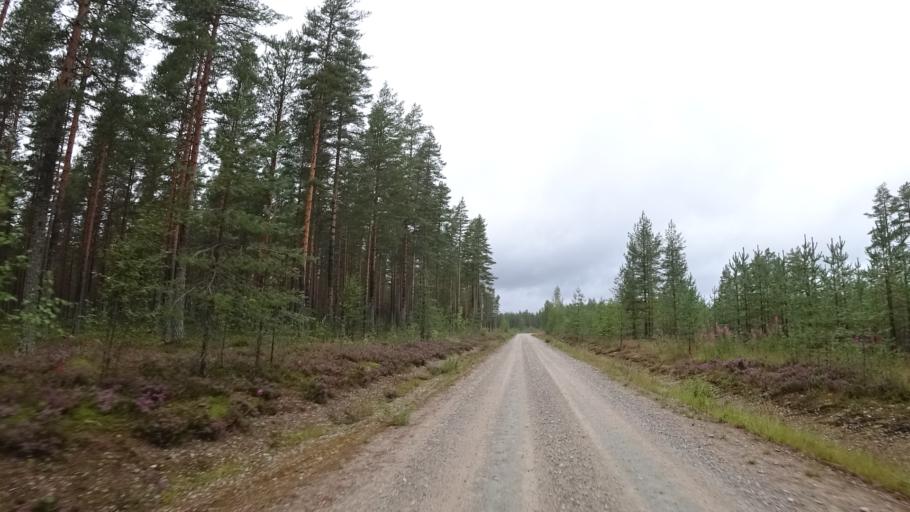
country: FI
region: North Karelia
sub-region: Pielisen Karjala
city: Lieksa
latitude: 63.5313
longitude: 30.0603
